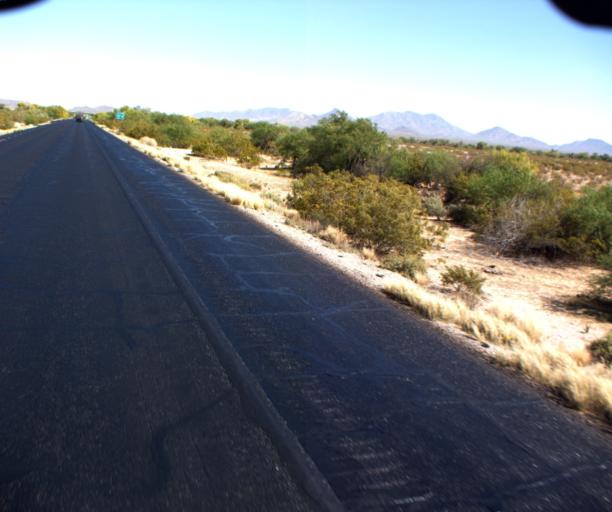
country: US
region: Arizona
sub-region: Pinal County
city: Maricopa
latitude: 32.8428
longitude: -112.2626
